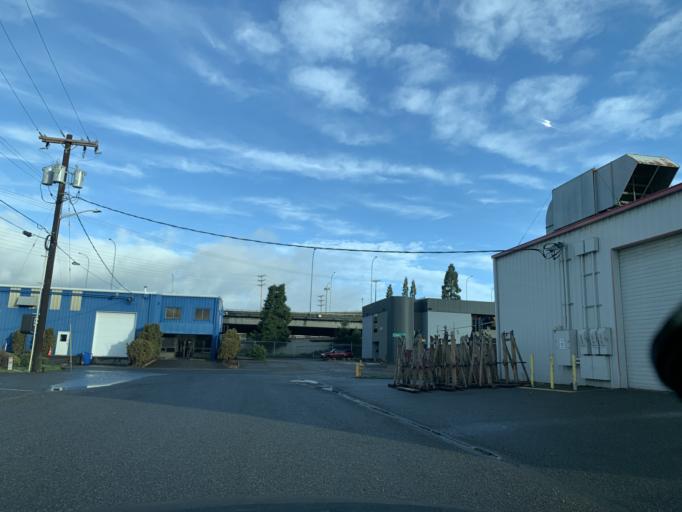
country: US
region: Washington
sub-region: King County
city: Seattle
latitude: 47.5703
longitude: -122.3240
